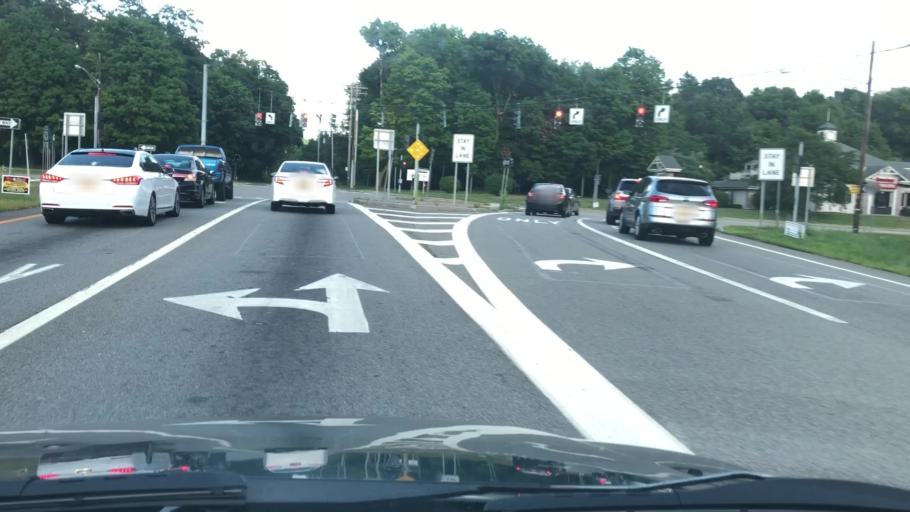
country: US
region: New York
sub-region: Dutchess County
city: Fishkill
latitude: 41.5221
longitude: -73.8902
